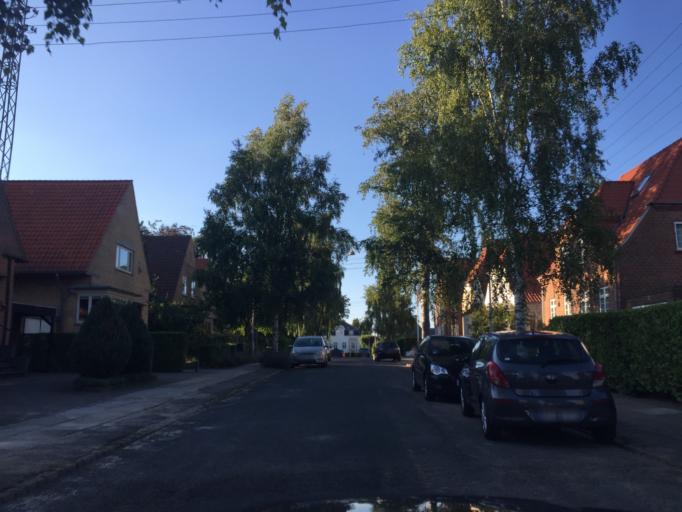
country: DK
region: South Denmark
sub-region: Odense Kommune
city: Odense
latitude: 55.3835
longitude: 10.3925
